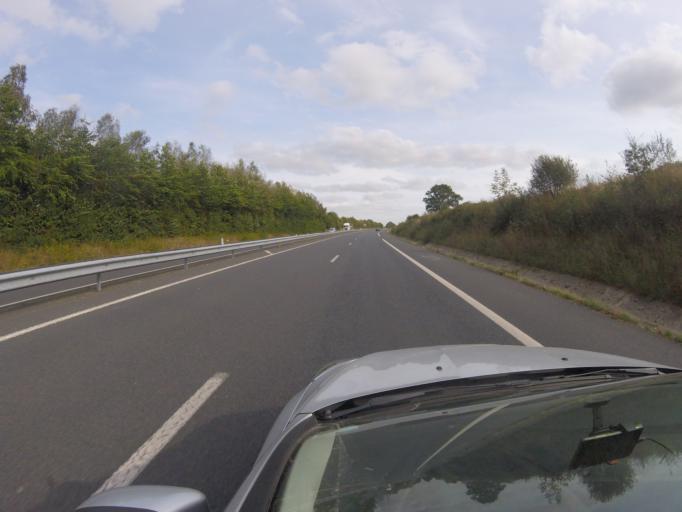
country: FR
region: Lower Normandy
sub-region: Departement de la Manche
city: Pont-Hebert
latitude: 49.1181
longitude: -1.1644
